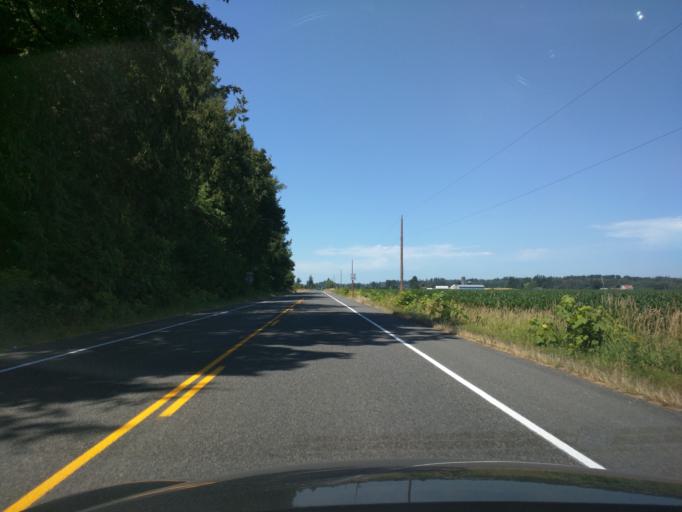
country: US
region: Washington
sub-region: Whatcom County
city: Lynden
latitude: 48.9648
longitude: -122.5140
